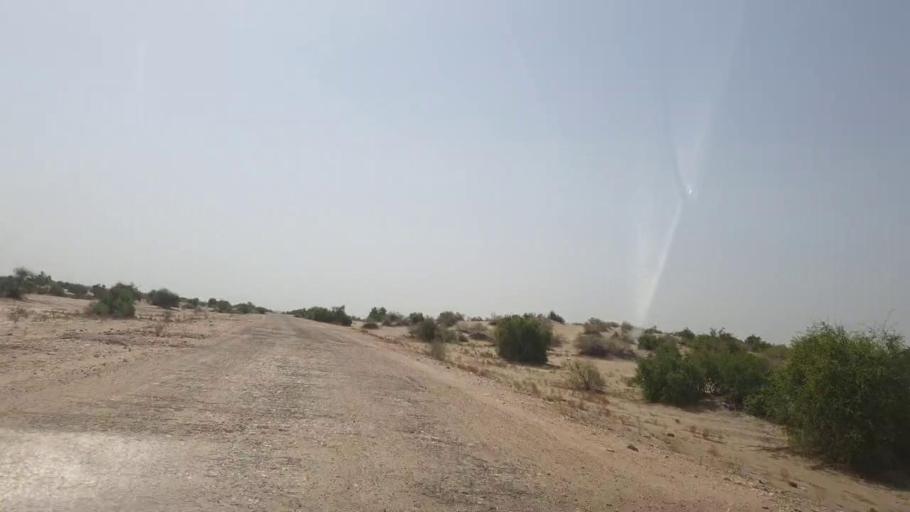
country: PK
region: Sindh
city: Rohri
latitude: 27.4353
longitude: 69.2475
